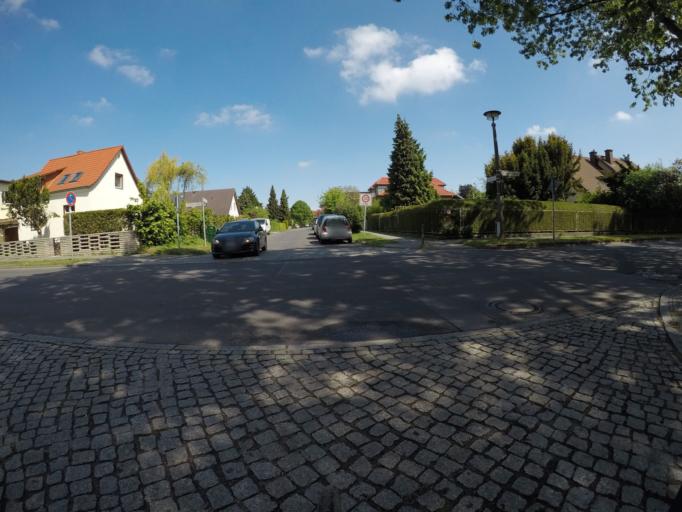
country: DE
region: Berlin
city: Biesdorf
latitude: 52.5162
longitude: 13.5479
